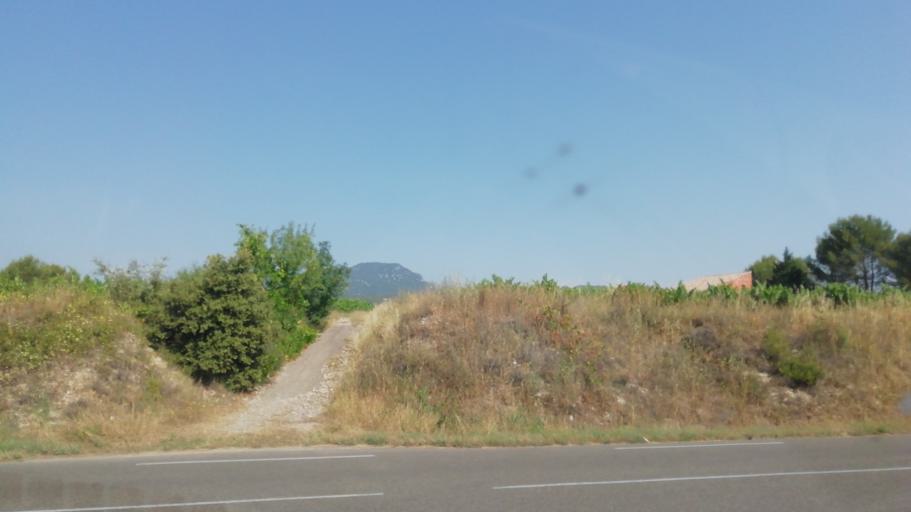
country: FR
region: Languedoc-Roussillon
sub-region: Departement de l'Herault
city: Saint-Mathieu-de-Treviers
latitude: 43.7437
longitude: 3.8559
